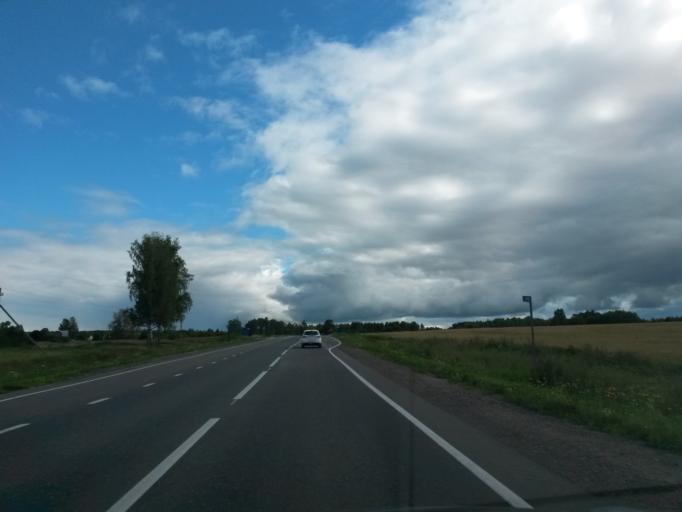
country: RU
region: Jaroslavl
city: Gavrilov-Yam
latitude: 57.3247
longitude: 39.9263
